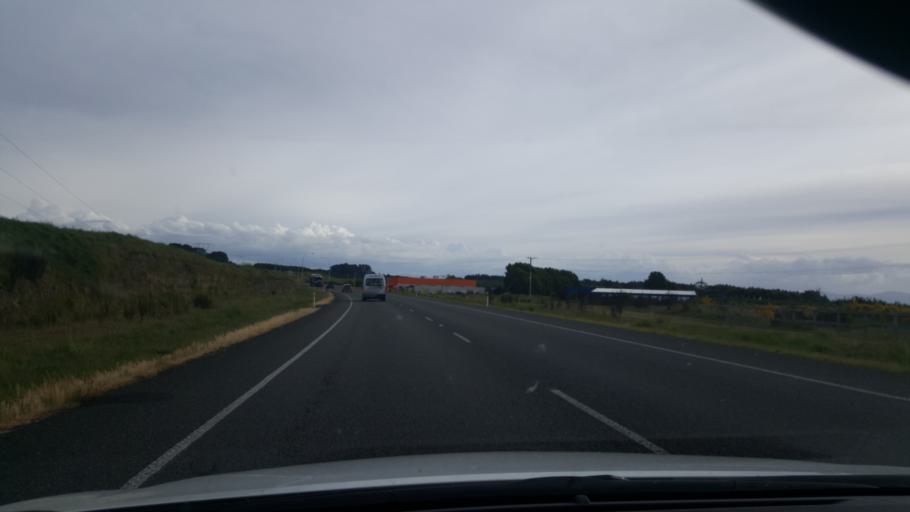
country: NZ
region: Waikato
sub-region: Taupo District
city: Taupo
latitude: -38.6991
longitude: 176.1122
